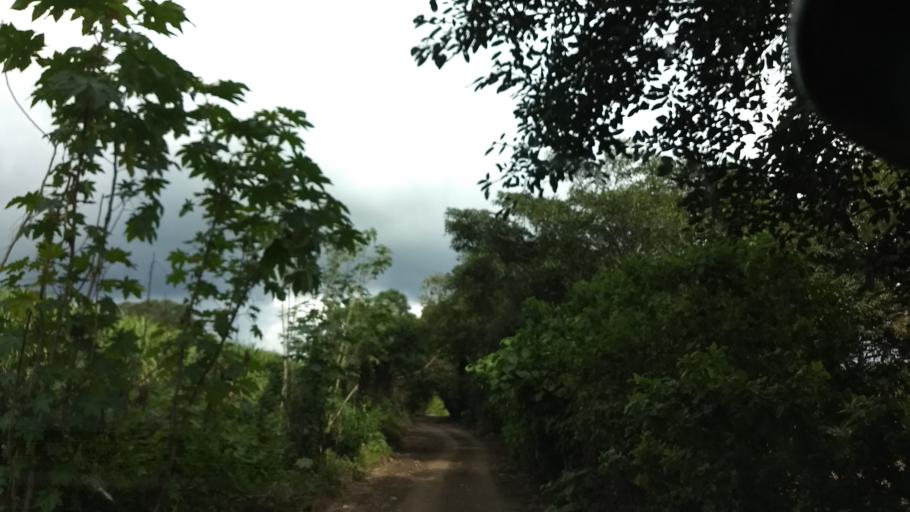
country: MX
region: Colima
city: Suchitlan
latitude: 19.4595
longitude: -103.7642
